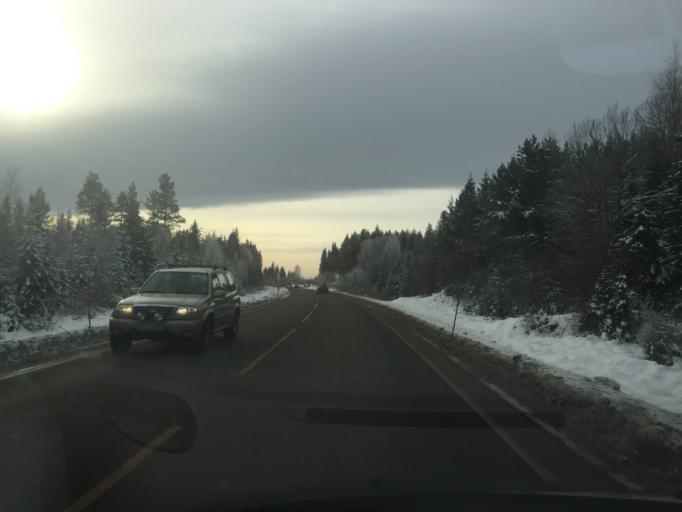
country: NO
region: Hedmark
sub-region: Elverum
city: Elverum
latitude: 60.9385
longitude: 11.6795
